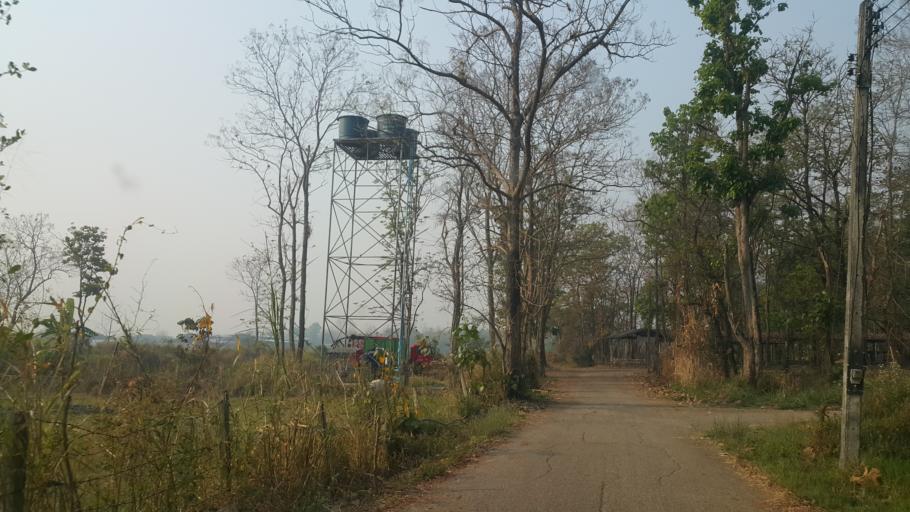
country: TH
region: Chiang Mai
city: Mae On
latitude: 18.7836
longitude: 99.2508
